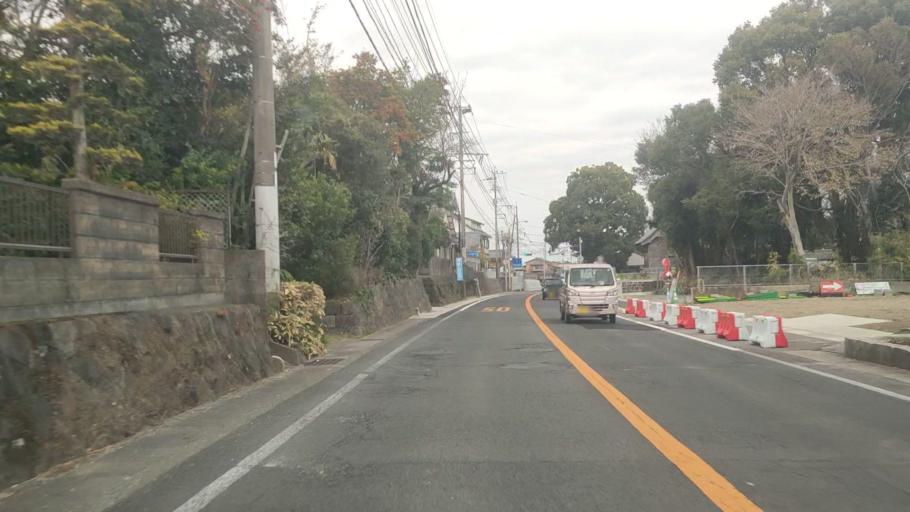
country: JP
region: Nagasaki
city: Shimabara
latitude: 32.8180
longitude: 130.3547
